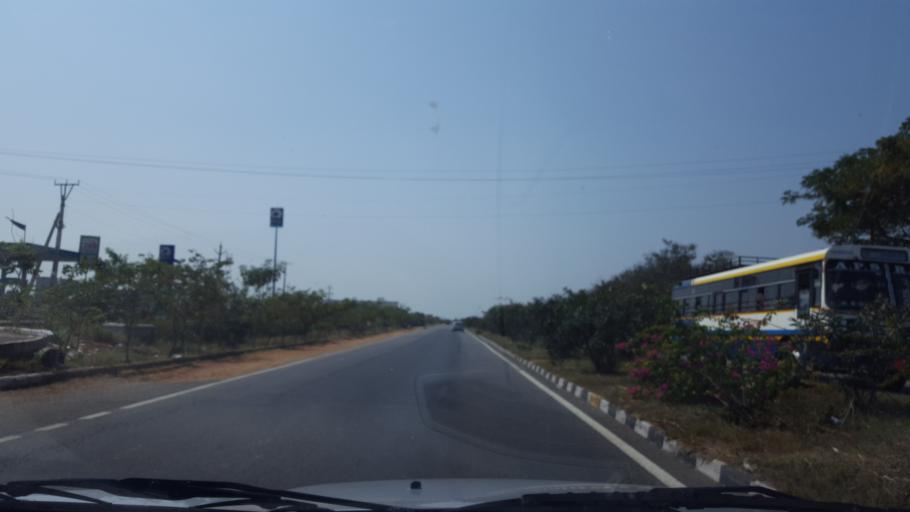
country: IN
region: Andhra Pradesh
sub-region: Guntur
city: Chilakalurupet
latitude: 16.0728
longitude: 80.1549
